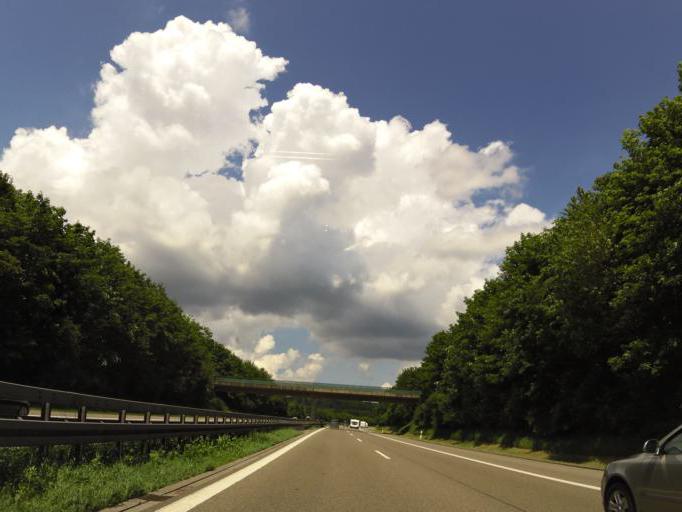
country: DE
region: Baden-Wuerttemberg
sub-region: Regierungsbezirk Stuttgart
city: Giengen an der Brenz
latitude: 48.6346
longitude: 10.2187
